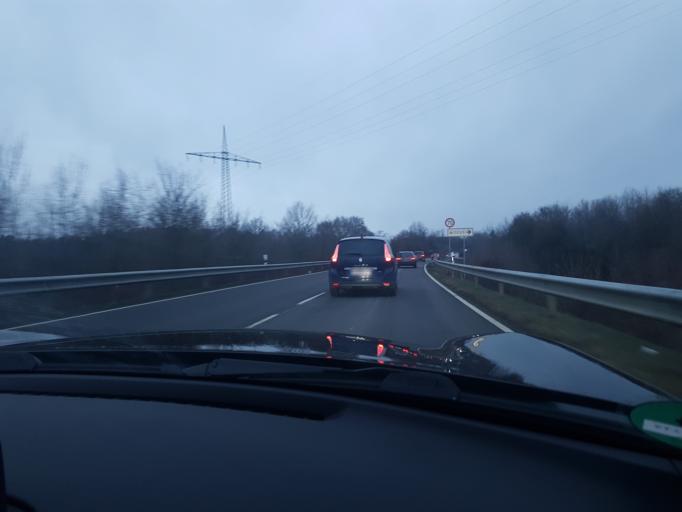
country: DE
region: Baden-Wuerttemberg
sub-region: Karlsruhe Region
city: Buchen
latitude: 49.5039
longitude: 9.3092
